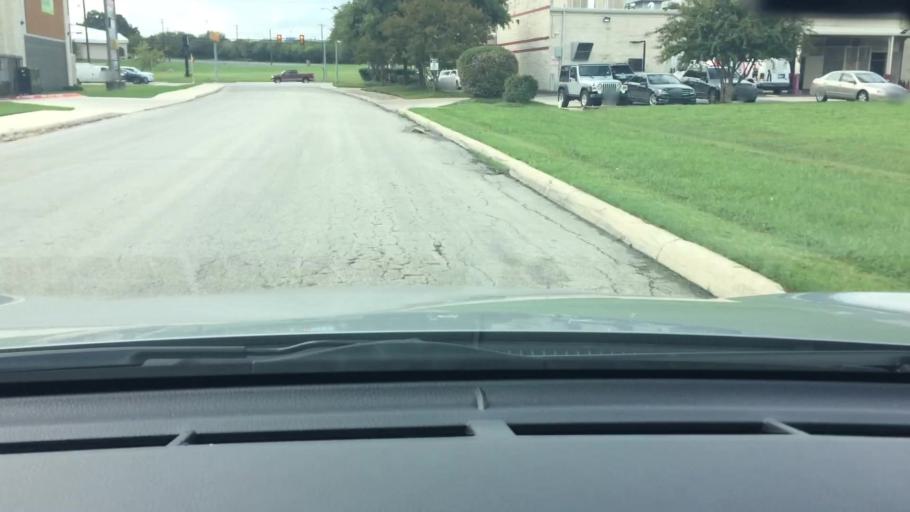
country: US
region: Texas
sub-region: Bexar County
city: Leon Valley
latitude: 29.5337
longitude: -98.5885
